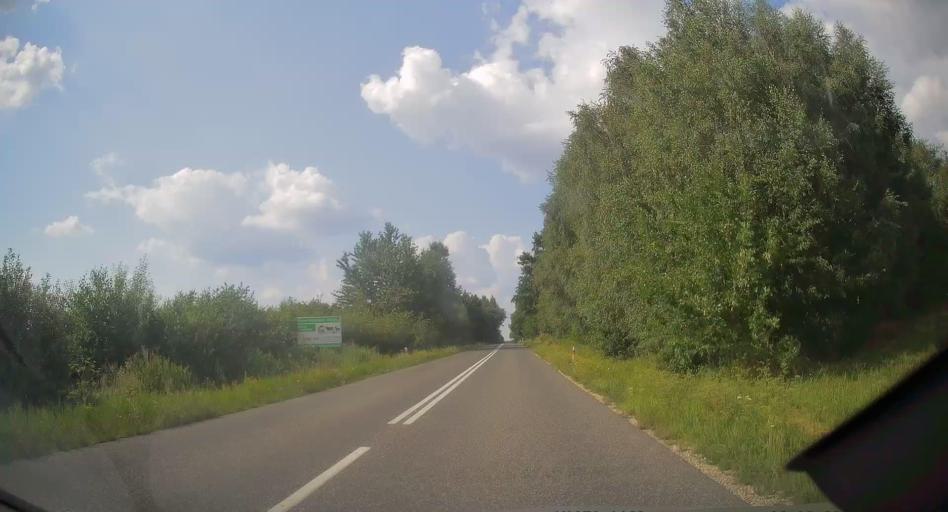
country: PL
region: Swietokrzyskie
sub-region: Powiat kielecki
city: Lopuszno
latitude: 50.9253
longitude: 20.2398
